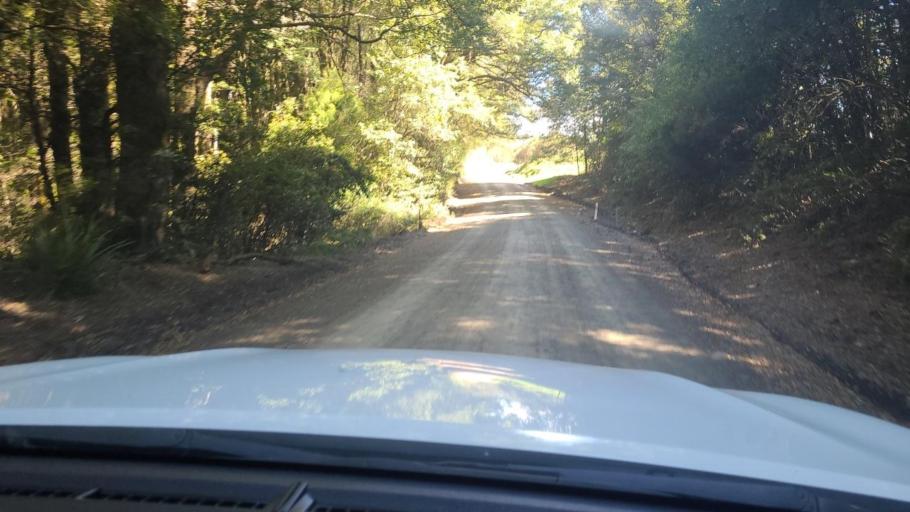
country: NZ
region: Hawke's Bay
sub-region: Napier City
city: Napier
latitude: -39.1203
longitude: 176.8106
